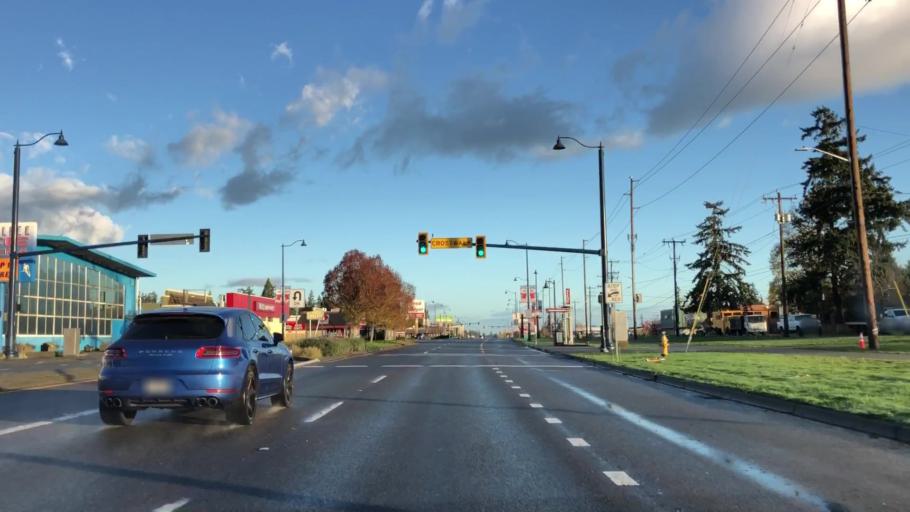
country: US
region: Washington
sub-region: King County
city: Shoreline
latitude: 47.7596
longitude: -122.3458
